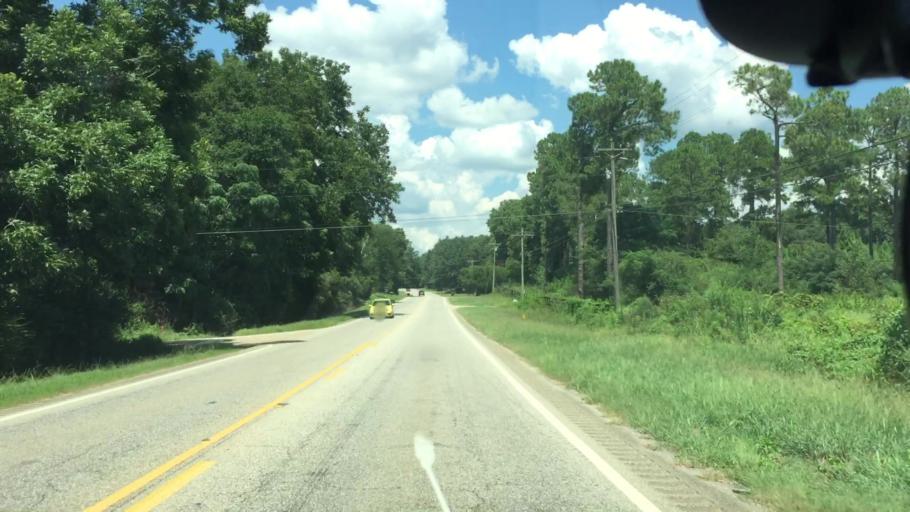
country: US
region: Alabama
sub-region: Pike County
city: Troy
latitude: 31.7241
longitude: -85.9591
